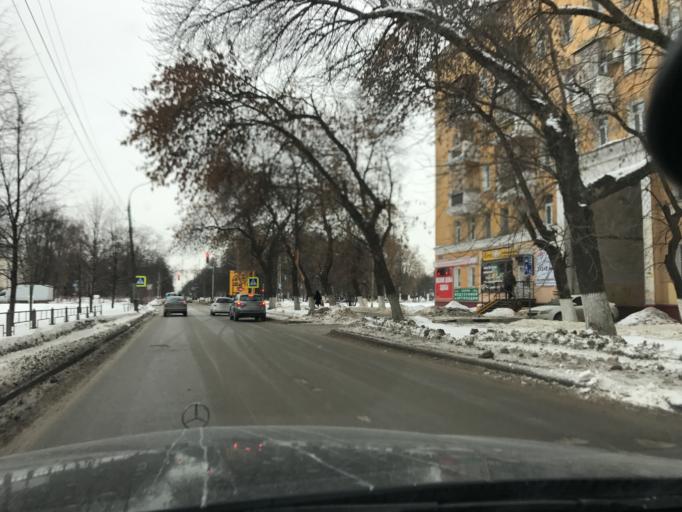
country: RU
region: Nizjnij Novgorod
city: Gorbatovka
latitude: 56.2463
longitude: 43.8490
